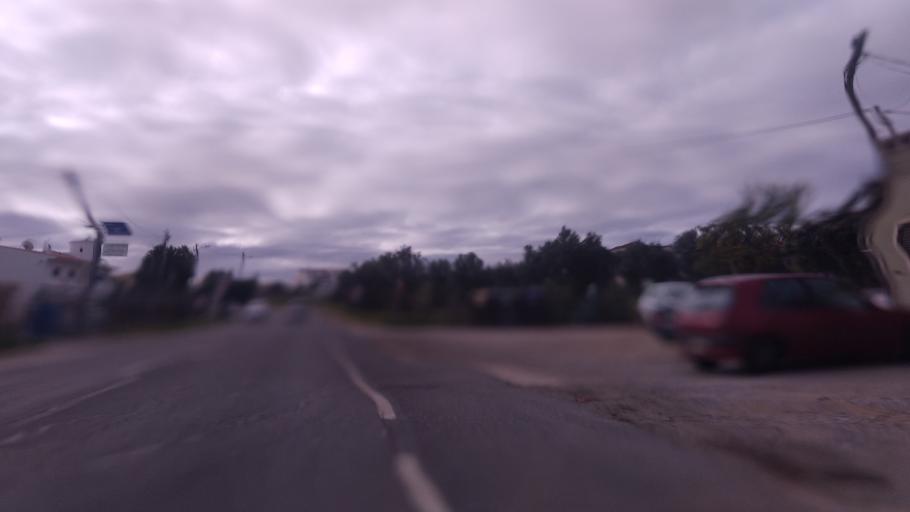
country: PT
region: Faro
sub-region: Faro
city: Faro
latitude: 37.0377
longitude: -7.9308
